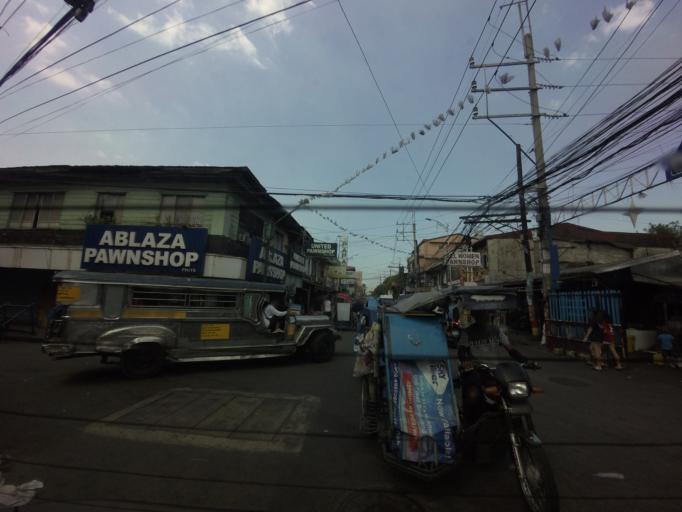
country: PH
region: Metro Manila
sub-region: City of Manila
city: Manila
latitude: 14.6178
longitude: 120.9691
